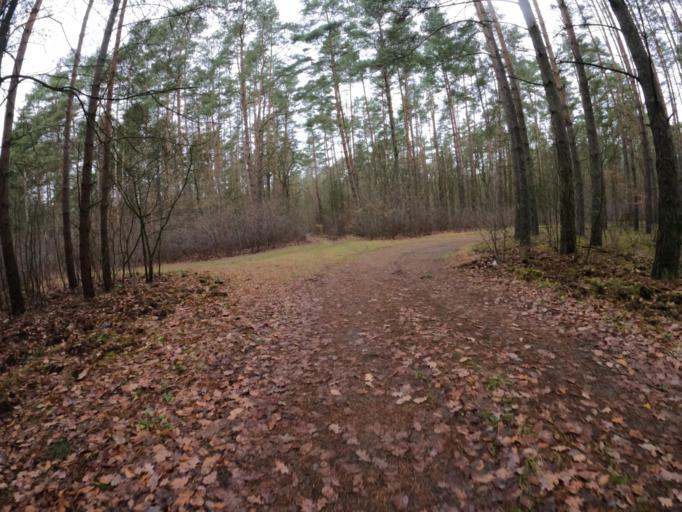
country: PL
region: West Pomeranian Voivodeship
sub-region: Powiat mysliborski
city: Debno
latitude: 52.7656
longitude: 14.7566
